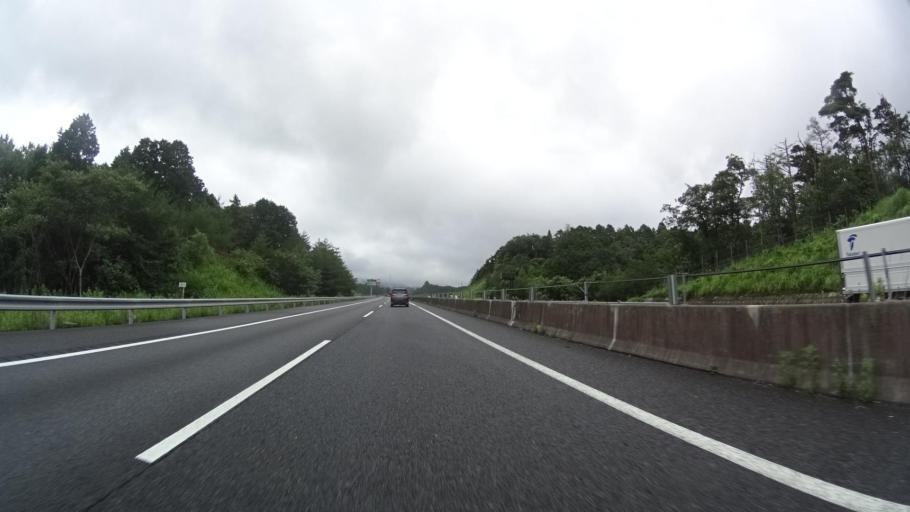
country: JP
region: Shiga Prefecture
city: Hino
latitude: 34.9155
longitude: 136.3126
